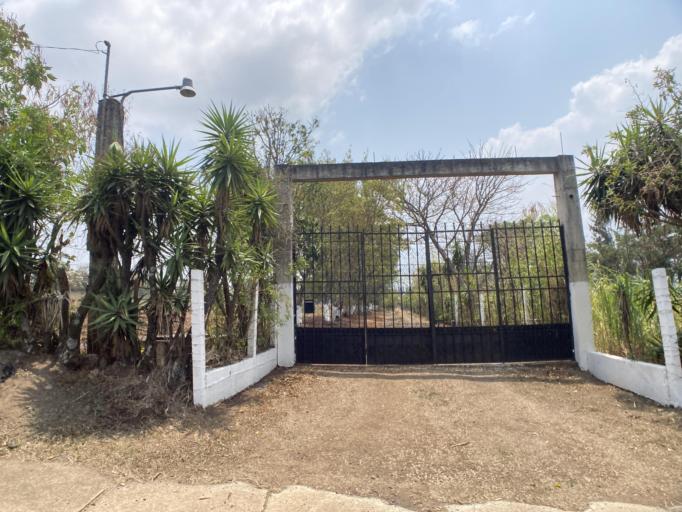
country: GT
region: Santa Rosa
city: Pueblo Nuevo Vinas
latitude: 14.3284
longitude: -90.5234
